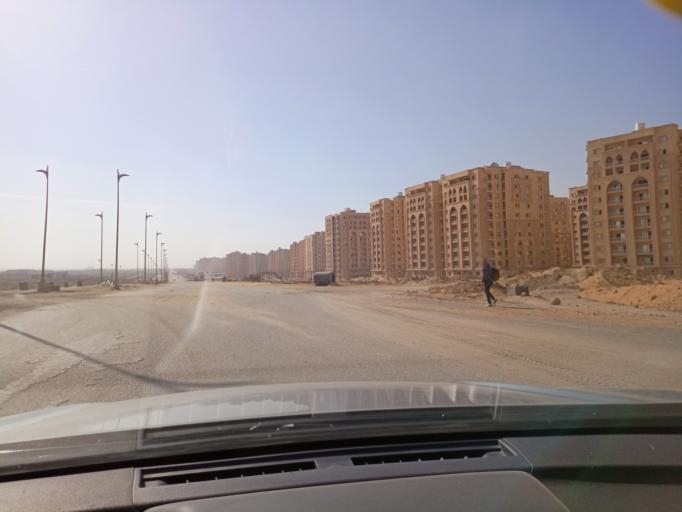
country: EG
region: Muhafazat al Qalyubiyah
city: Al Khankah
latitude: 30.0242
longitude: 31.6736
